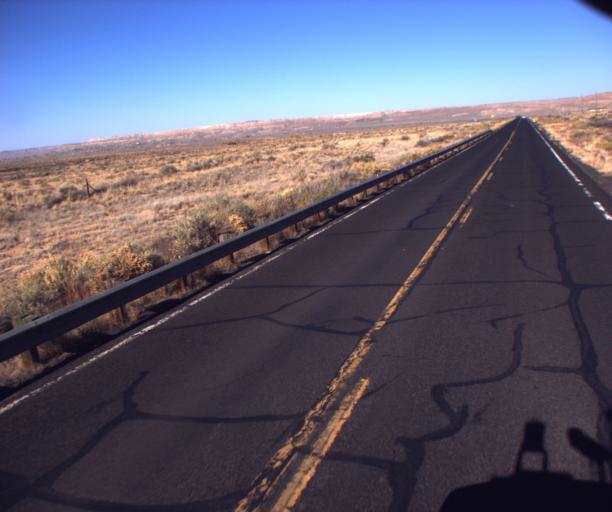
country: US
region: Arizona
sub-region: Navajo County
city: First Mesa
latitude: 35.8347
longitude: -110.2981
